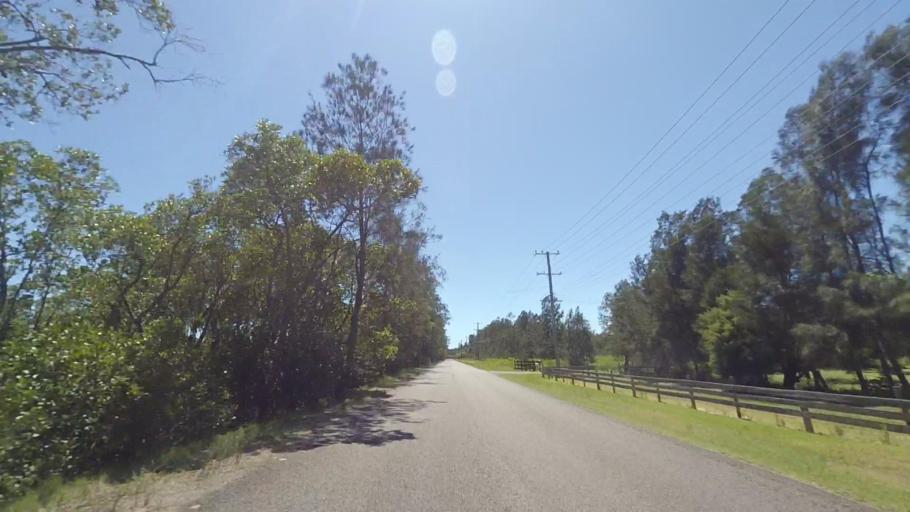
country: AU
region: New South Wales
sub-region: Port Stephens Shire
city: Medowie
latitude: -32.7793
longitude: 151.9608
